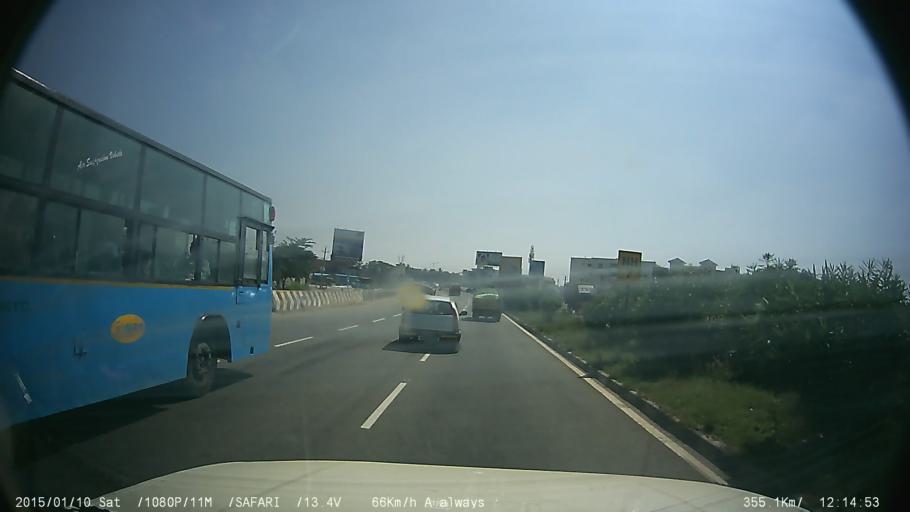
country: IN
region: Karnataka
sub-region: Bangalore Urban
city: Anekal
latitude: 12.8052
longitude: 77.7003
